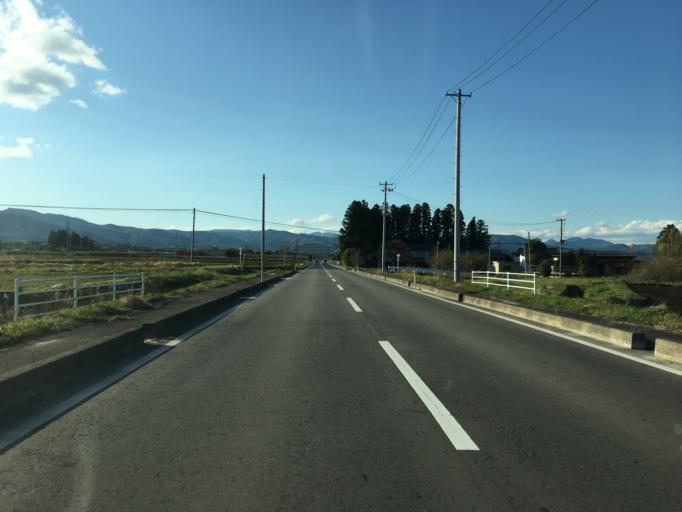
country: JP
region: Fukushima
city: Fukushima-shi
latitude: 37.7185
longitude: 140.3934
